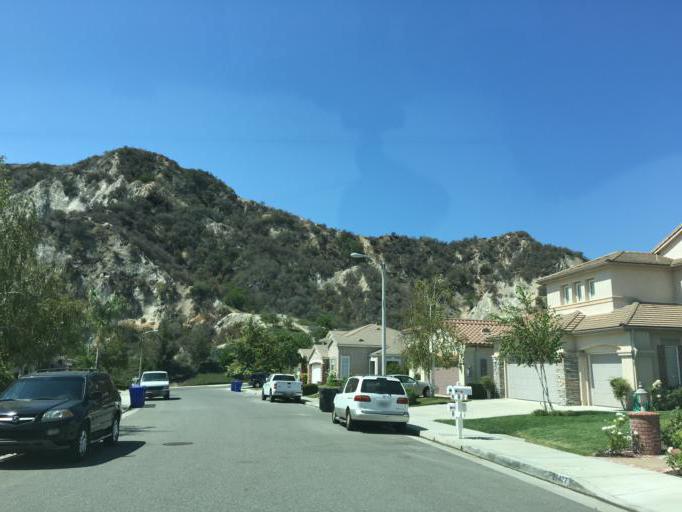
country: US
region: California
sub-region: Los Angeles County
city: Santa Clarita
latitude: 34.3850
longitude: -118.5969
